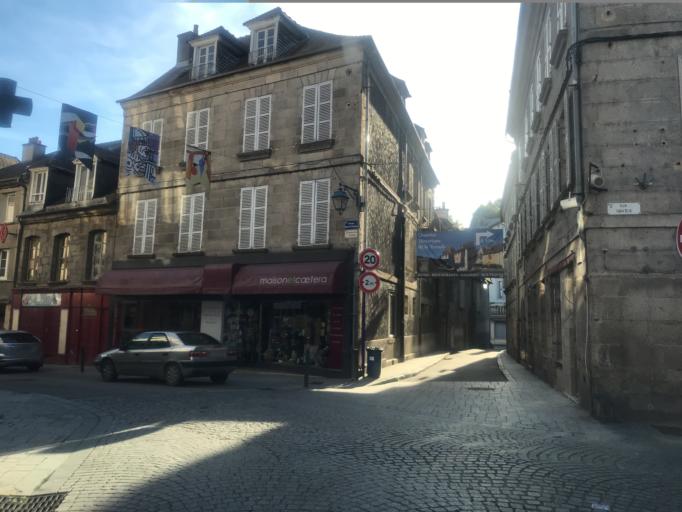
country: FR
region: Limousin
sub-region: Departement de la Creuse
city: Aubusson
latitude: 45.9566
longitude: 2.1677
